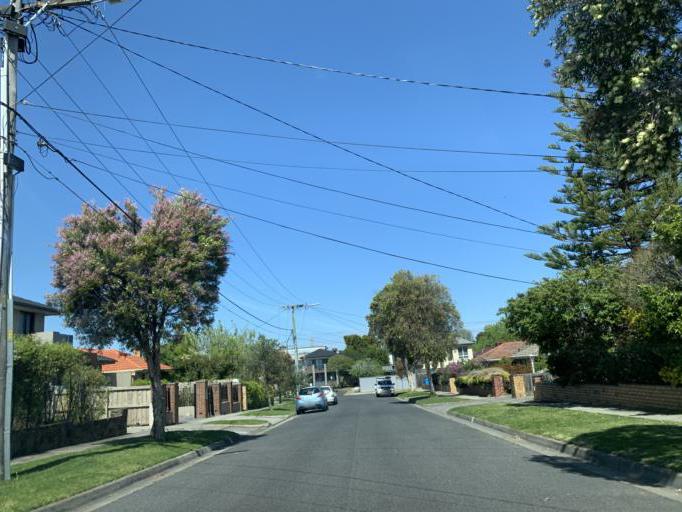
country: AU
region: Victoria
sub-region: Bayside
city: Highett
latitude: -37.9457
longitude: 145.0378
